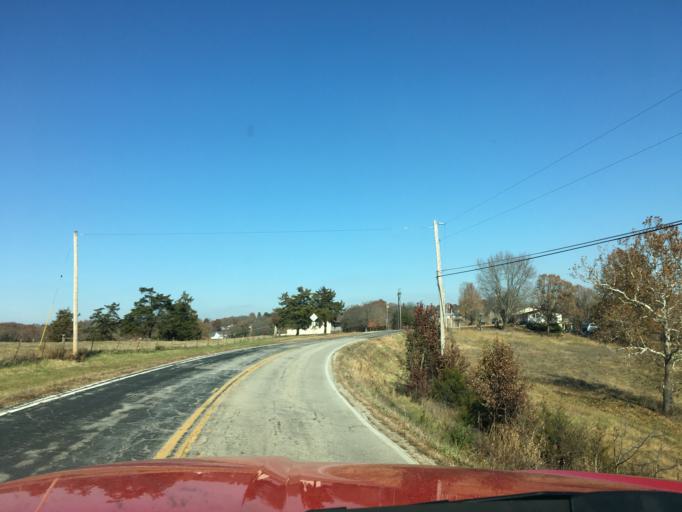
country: US
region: Missouri
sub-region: Cole County
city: Wardsville
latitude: 38.4746
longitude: -92.1781
